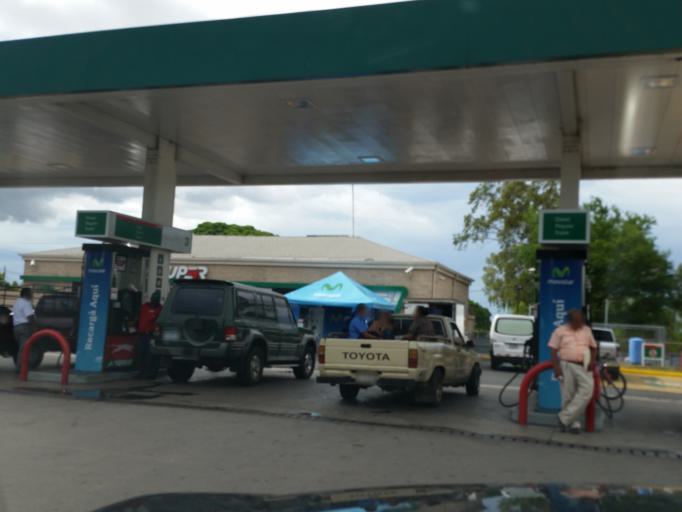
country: NI
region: Managua
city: Managua
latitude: 12.1258
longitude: -86.2839
